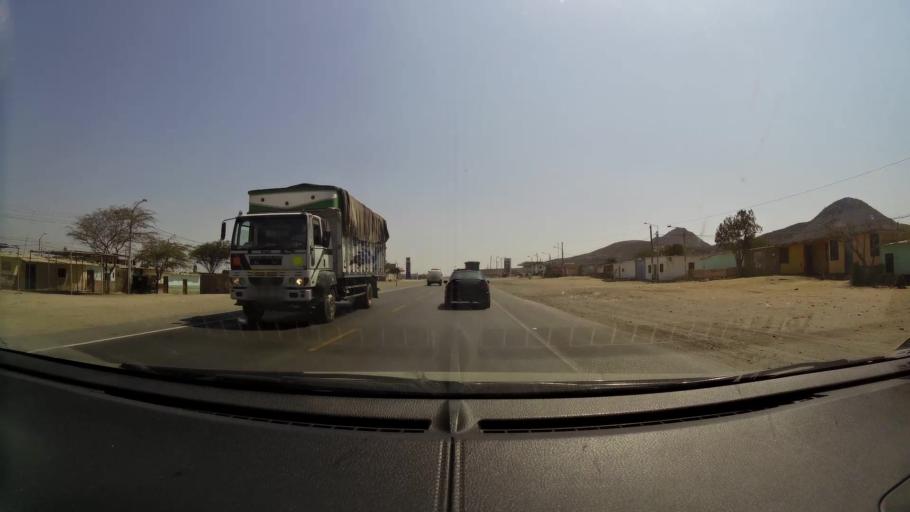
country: PE
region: Lambayeque
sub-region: Provincia de Chiclayo
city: Mocupe
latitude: -6.9784
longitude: -79.6501
